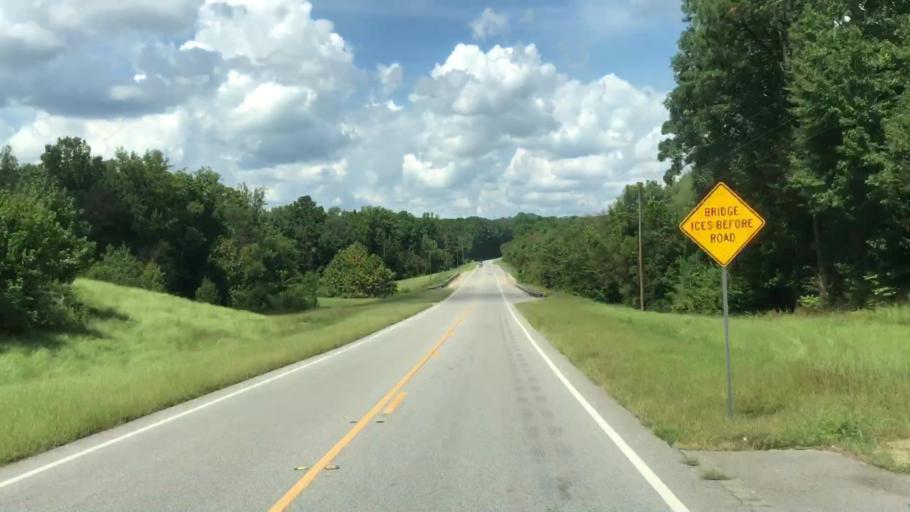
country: US
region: Georgia
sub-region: Greene County
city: Greensboro
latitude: 33.6689
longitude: -83.2592
